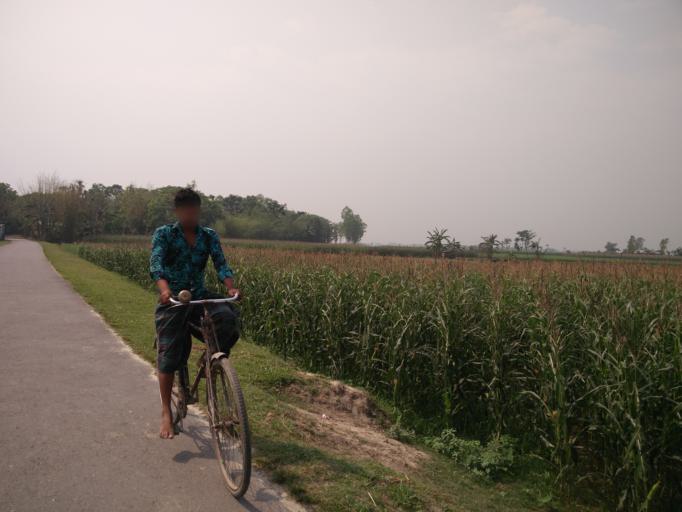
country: BD
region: Dhaka
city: Muktagacha
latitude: 24.9011
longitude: 90.2590
